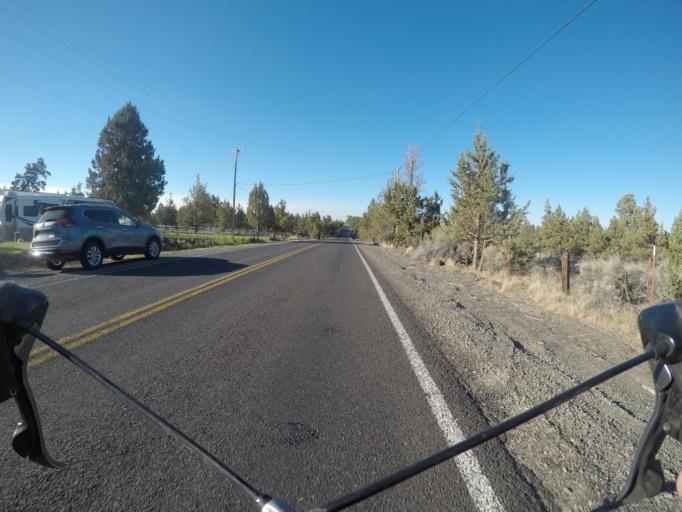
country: US
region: Oregon
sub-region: Deschutes County
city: Redmond
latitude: 44.2523
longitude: -121.2396
